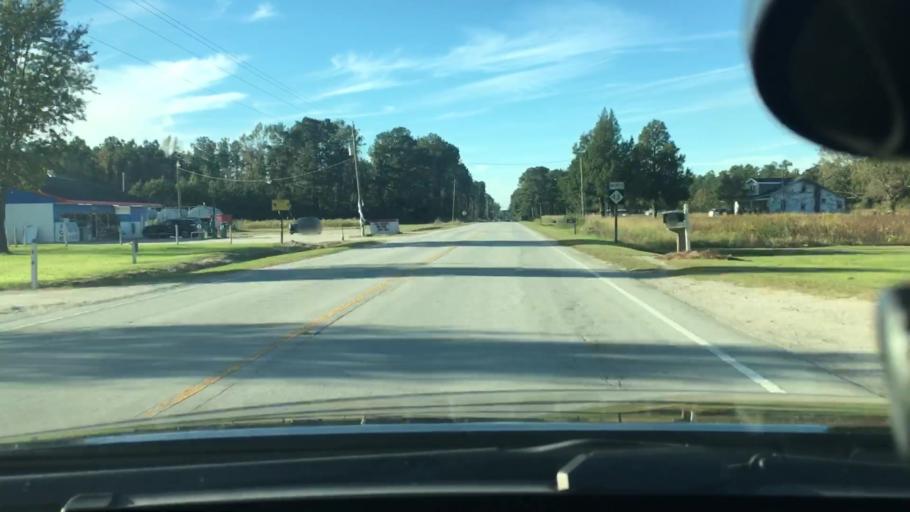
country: US
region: North Carolina
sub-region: Craven County
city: Vanceboro
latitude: 35.3413
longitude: -77.1781
